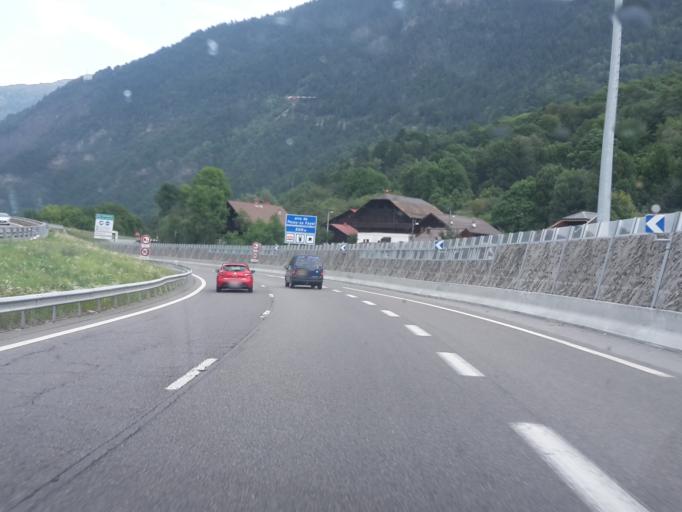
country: FR
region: Rhone-Alpes
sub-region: Departement de la Haute-Savoie
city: Saint-Gervais-les-Bains
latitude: 45.9097
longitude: 6.7113
